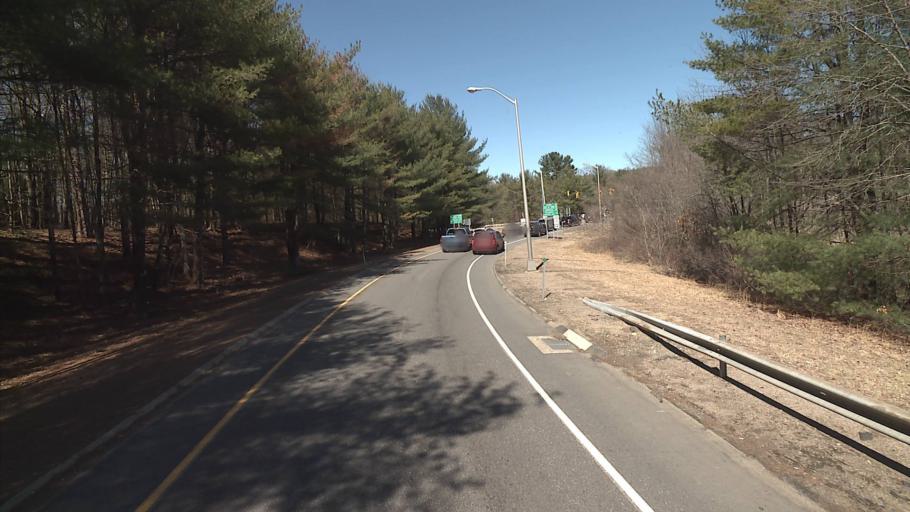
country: US
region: Connecticut
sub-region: Windham County
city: Willimantic
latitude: 41.7319
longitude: -72.2030
